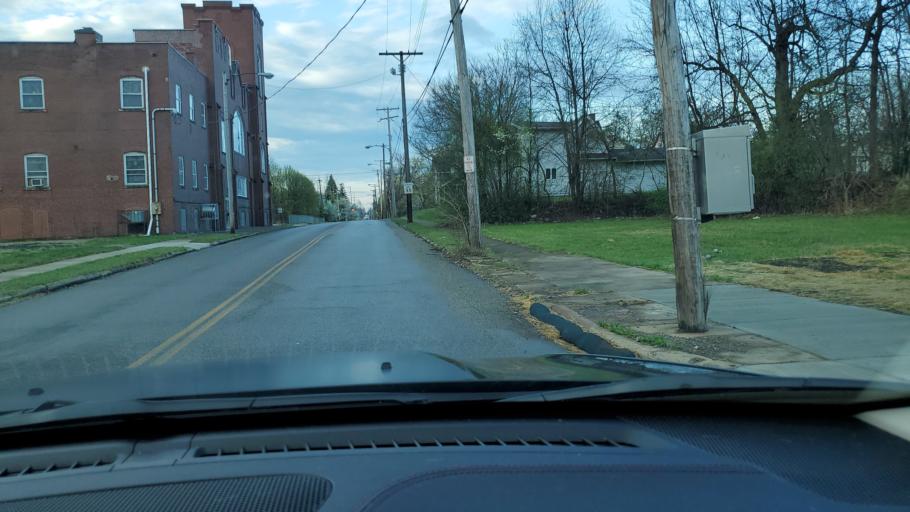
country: US
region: Ohio
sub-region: Mahoning County
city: Youngstown
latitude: 41.0936
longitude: -80.6640
